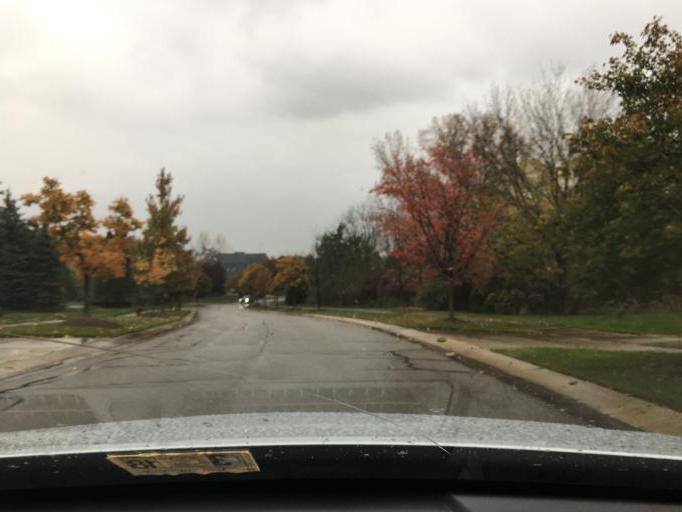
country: US
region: Michigan
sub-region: Oakland County
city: Auburn Hills
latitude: 42.7168
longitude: -83.1988
